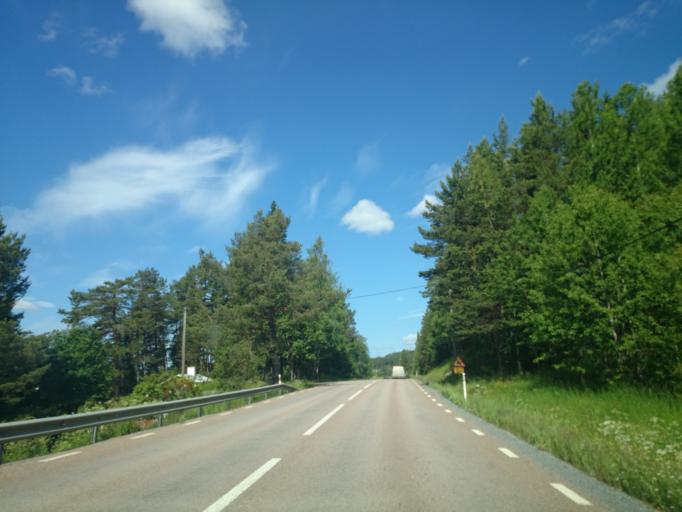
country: SE
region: Jaemtland
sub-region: OEstersunds Kommun
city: Brunflo
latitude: 63.0143
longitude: 14.9501
